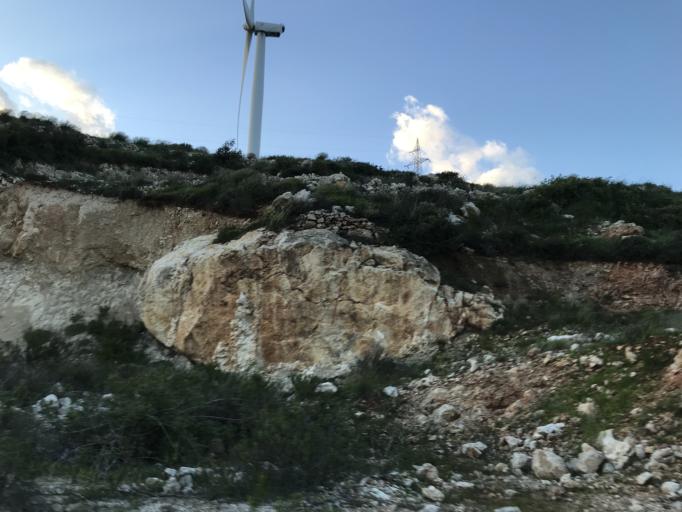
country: TR
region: Hatay
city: Buyukcat
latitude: 36.0968
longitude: 36.0407
